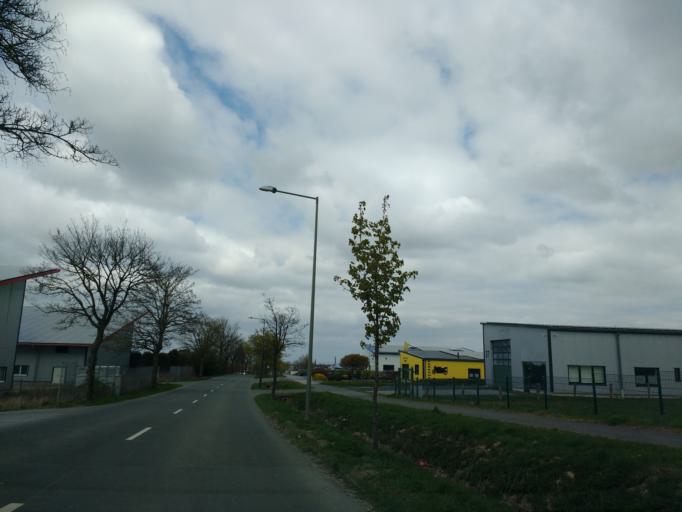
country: DE
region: North Rhine-Westphalia
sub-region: Regierungsbezirk Detmold
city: Wunnenberg
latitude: 51.5685
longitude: 8.7157
